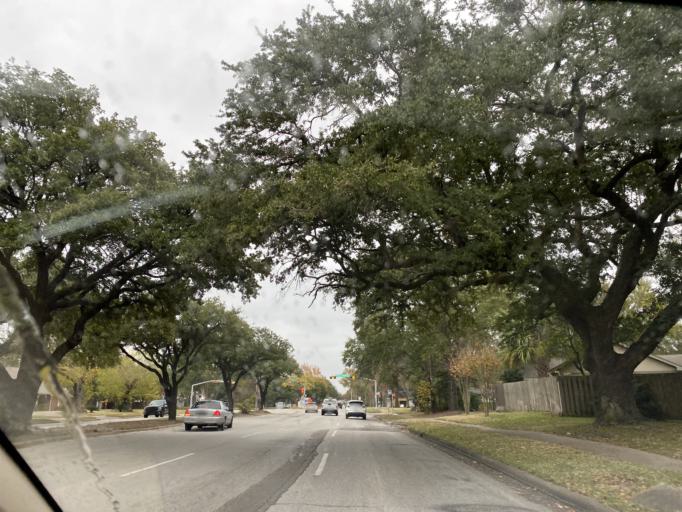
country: US
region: Texas
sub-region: Harris County
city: Piney Point Village
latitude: 29.7296
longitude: -95.5073
